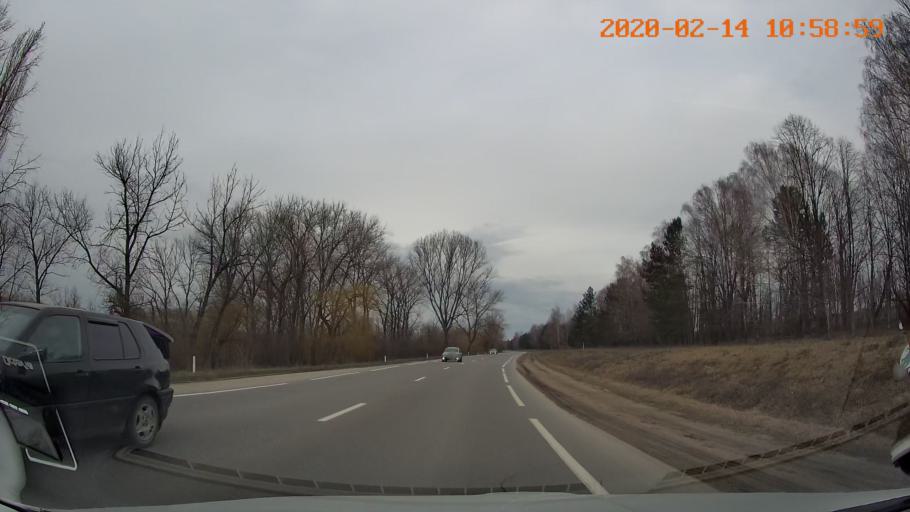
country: MD
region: Raionul Edinet
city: Edinet
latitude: 48.1374
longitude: 27.3573
